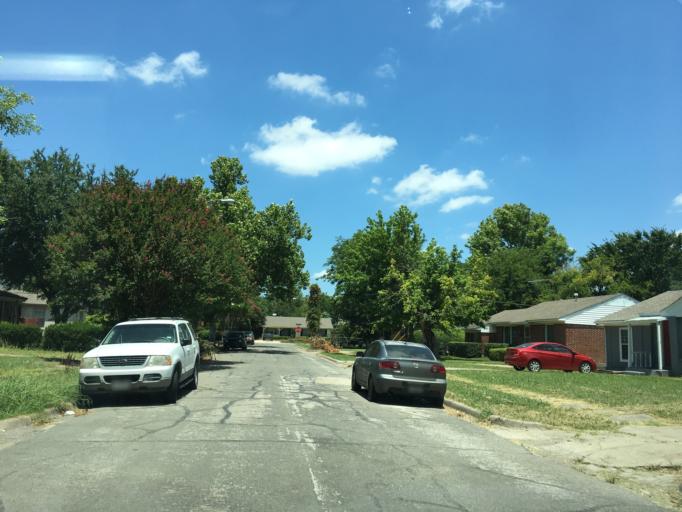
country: US
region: Texas
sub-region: Dallas County
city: Garland
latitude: 32.8487
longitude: -96.6719
